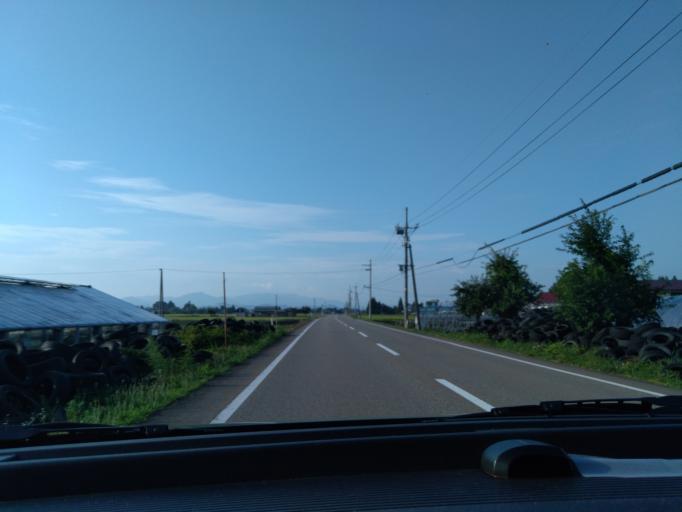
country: JP
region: Akita
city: Kakunodatemachi
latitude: 39.5114
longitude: 140.5590
